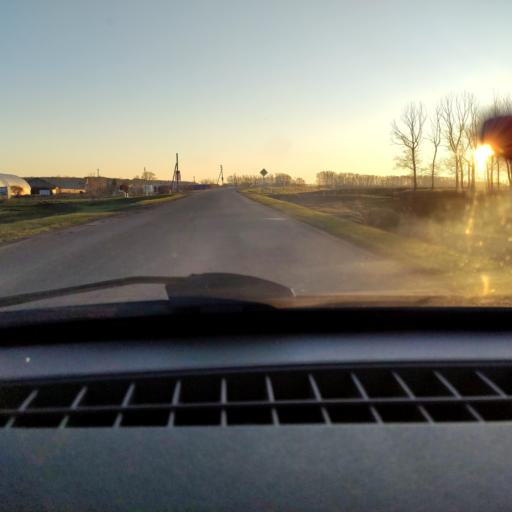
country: RU
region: Bashkortostan
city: Avdon
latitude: 54.5487
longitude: 55.6569
